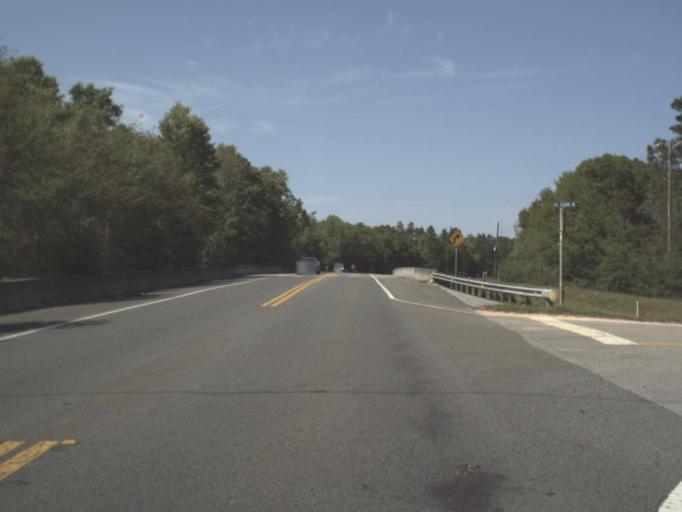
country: US
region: Florida
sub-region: Okaloosa County
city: Crestview
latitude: 30.7340
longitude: -86.6539
